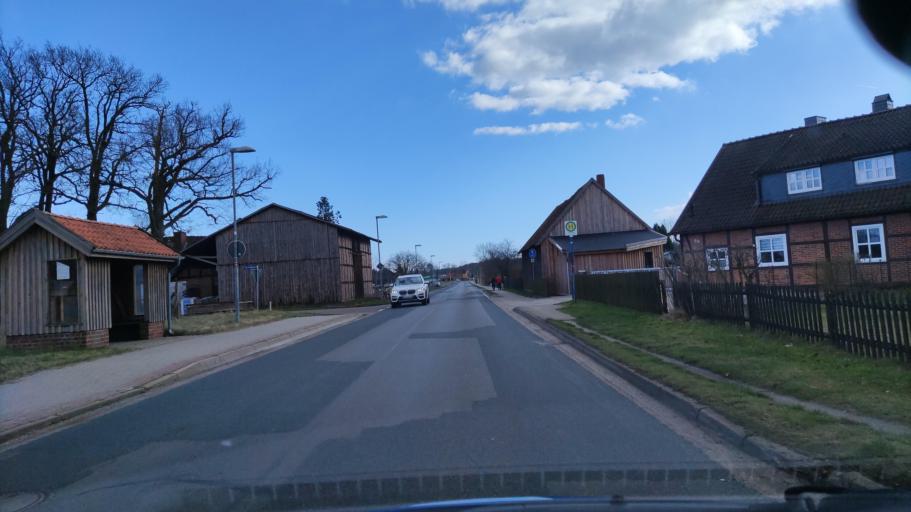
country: DE
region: Lower Saxony
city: Beedenbostel
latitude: 52.6358
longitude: 10.2158
